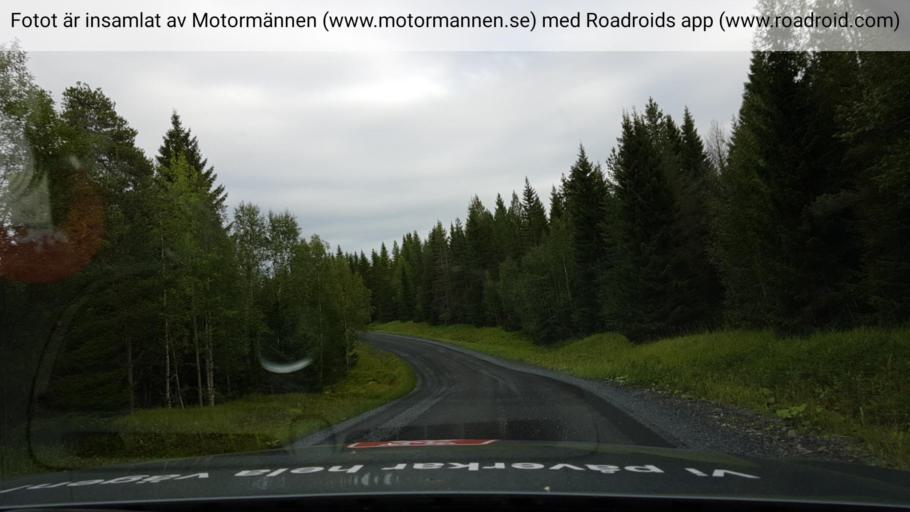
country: SE
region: Jaemtland
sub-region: Krokoms Kommun
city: Valla
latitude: 63.3675
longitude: 13.8871
